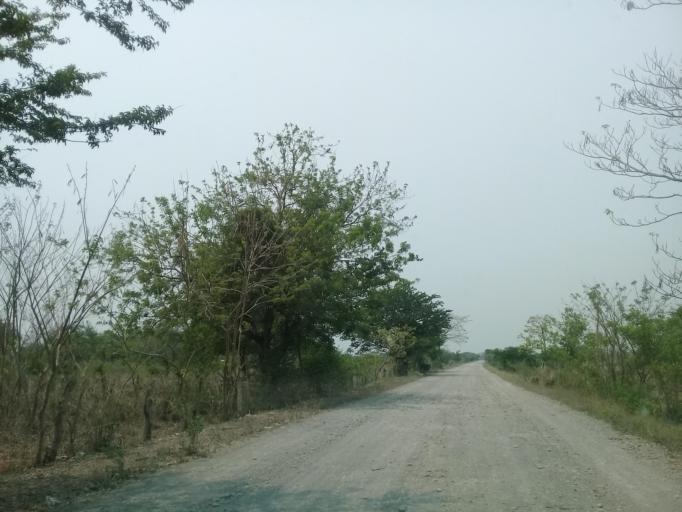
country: MX
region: Veracruz
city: Jamapa
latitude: 18.9359
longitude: -96.2168
